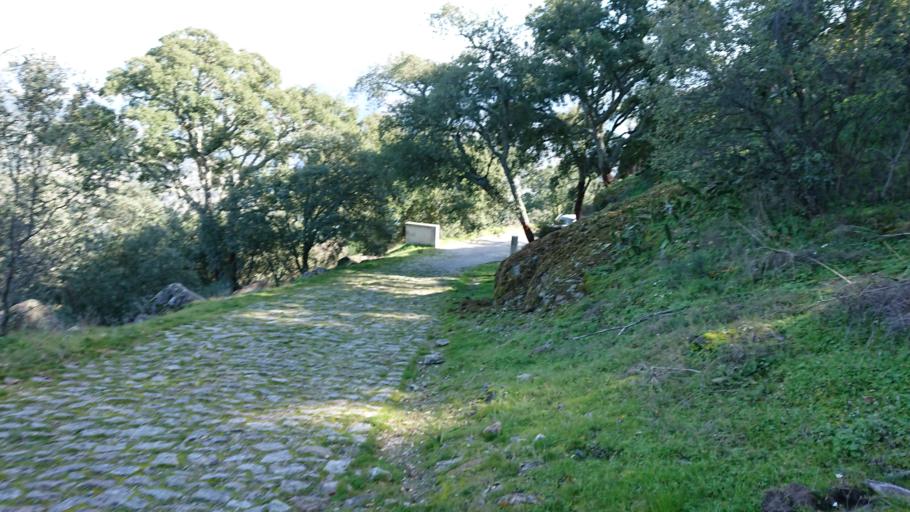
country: PT
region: Viseu
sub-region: Sao Joao da Pesqueira
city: Sao Joao da Pesqueira
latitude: 41.1520
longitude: -7.3663
